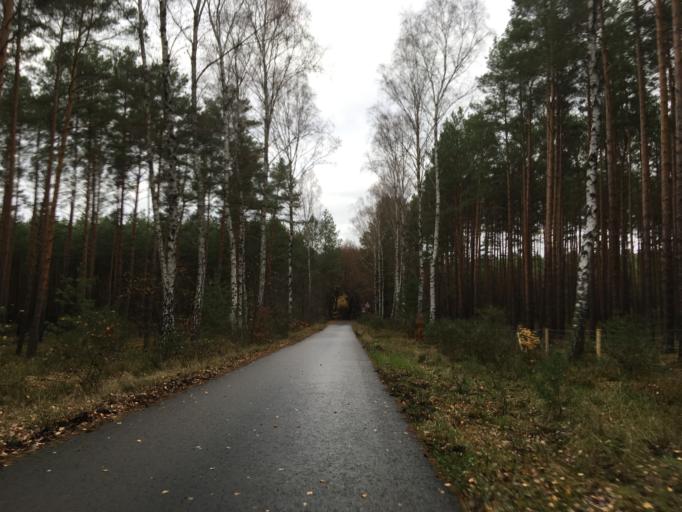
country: DE
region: Brandenburg
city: Jamlitz
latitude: 52.0563
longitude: 14.4812
